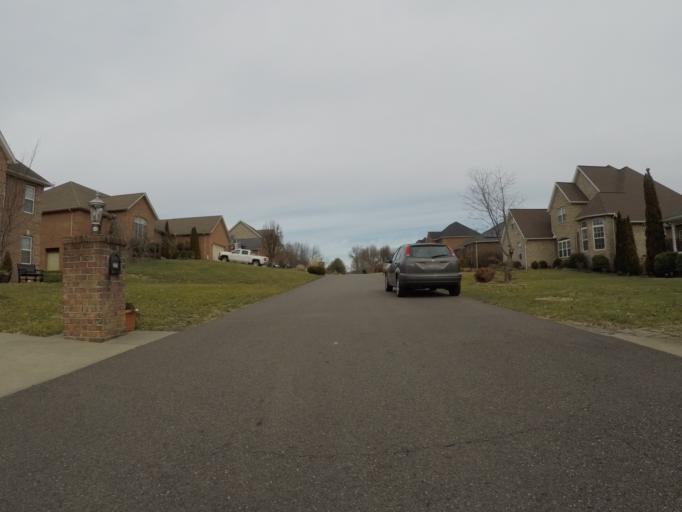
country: US
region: West Virginia
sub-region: Cabell County
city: Pea Ridge
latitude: 38.4471
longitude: -82.3495
